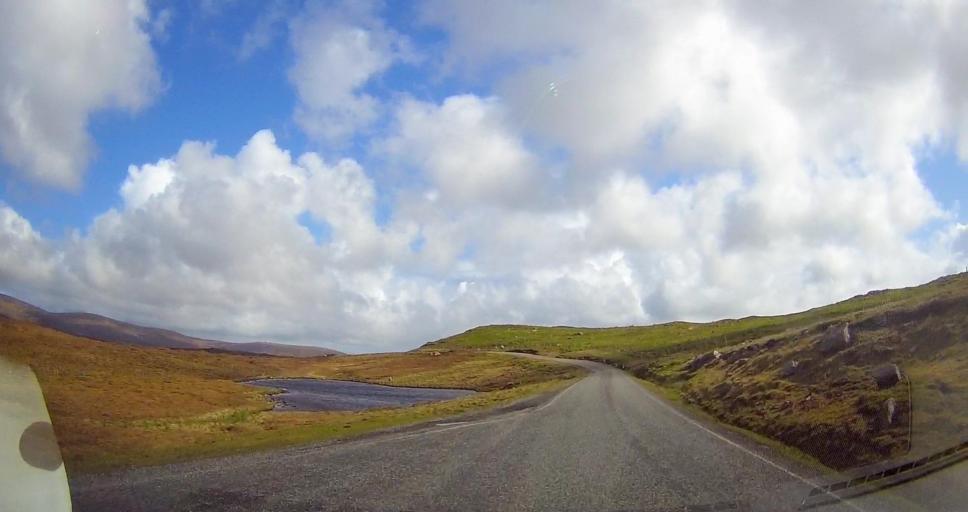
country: GB
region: Scotland
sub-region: Shetland Islands
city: Lerwick
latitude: 60.4824
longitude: -1.4050
